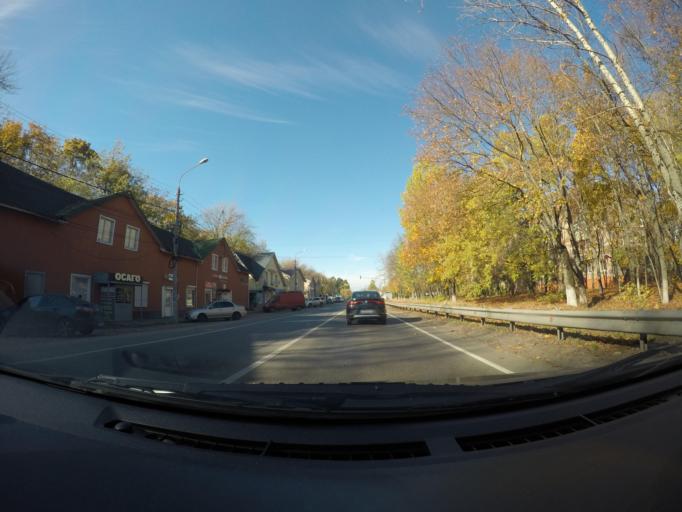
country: RU
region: Moskovskaya
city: Udel'naya
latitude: 55.6263
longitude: 38.0039
